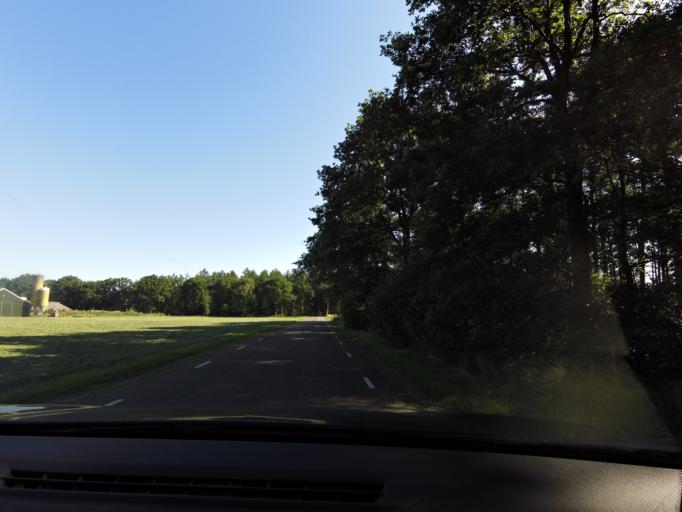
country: NL
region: Overijssel
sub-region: Gemeente Raalte
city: Raalte
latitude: 52.3026
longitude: 6.3065
